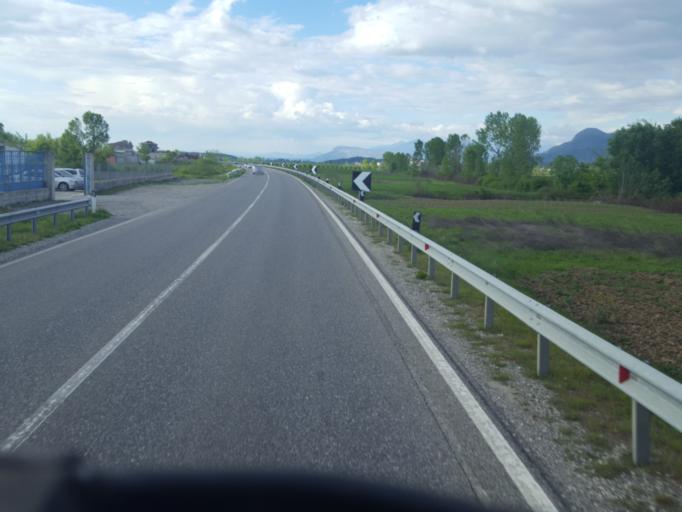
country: AL
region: Lezhe
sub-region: Rrethi i Lezhes
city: Balldreni i Ri
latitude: 41.8628
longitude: 19.6378
